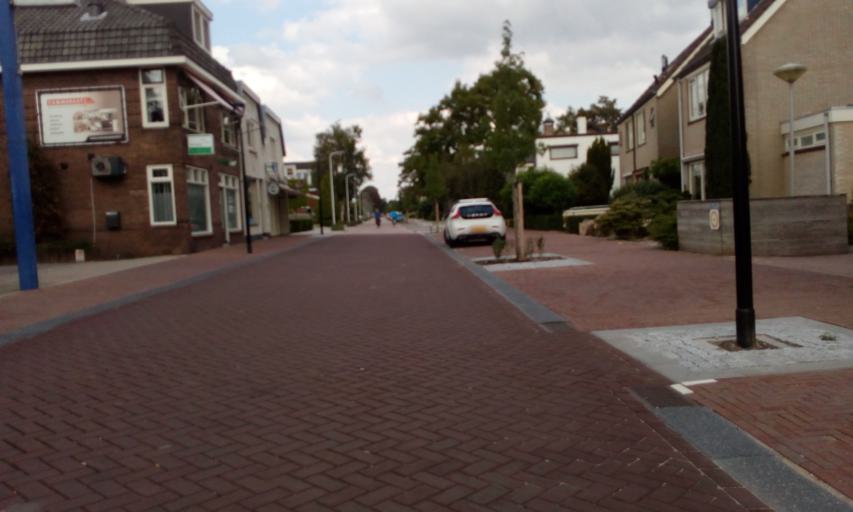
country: NL
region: South Holland
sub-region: Gemeente Waddinxveen
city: Groenswaard
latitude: 52.0470
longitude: 4.6415
